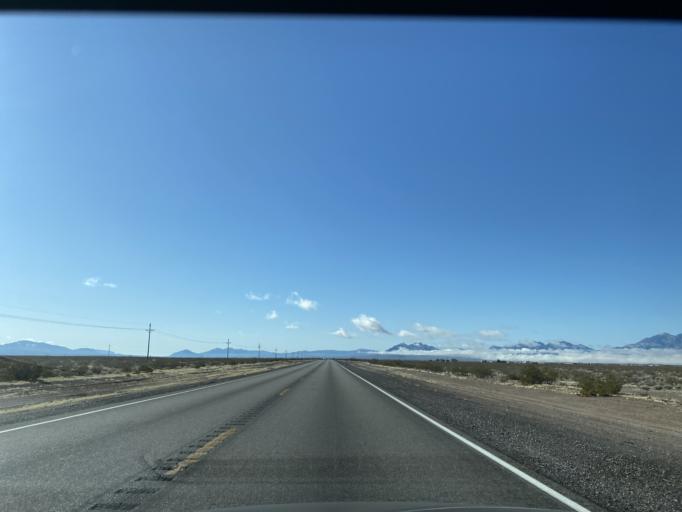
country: US
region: Nevada
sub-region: Nye County
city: Beatty
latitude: 36.5807
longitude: -116.4115
